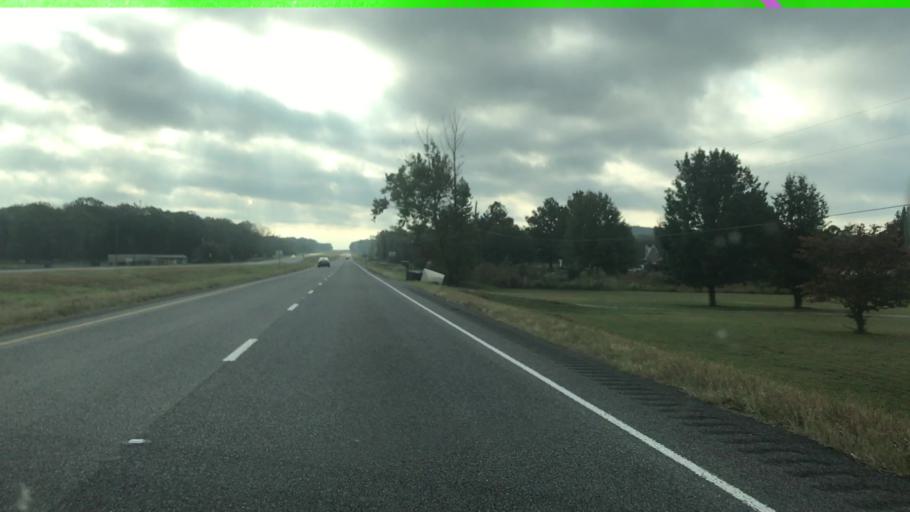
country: US
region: Alabama
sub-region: Morgan County
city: Danville
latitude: 34.4116
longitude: -87.1523
